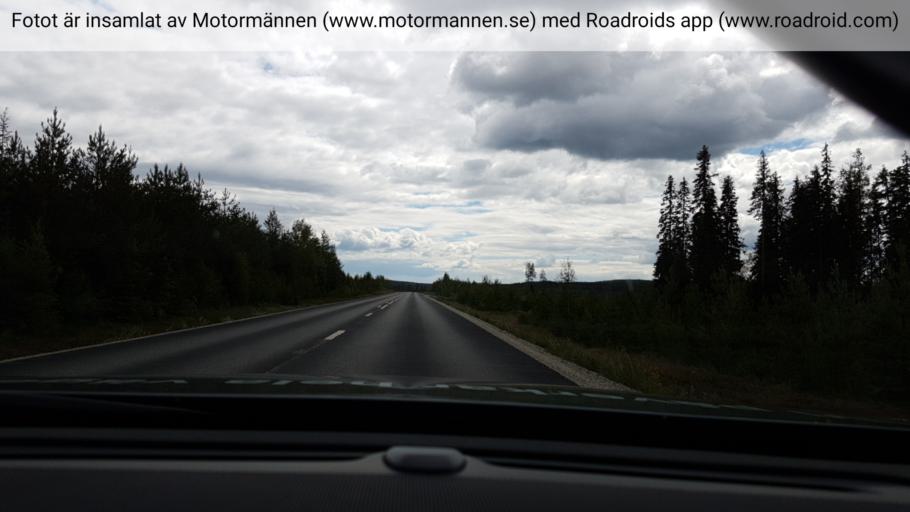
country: SE
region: Vaesterbotten
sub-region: Vindelns Kommun
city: Vindeln
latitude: 64.0677
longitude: 19.6373
